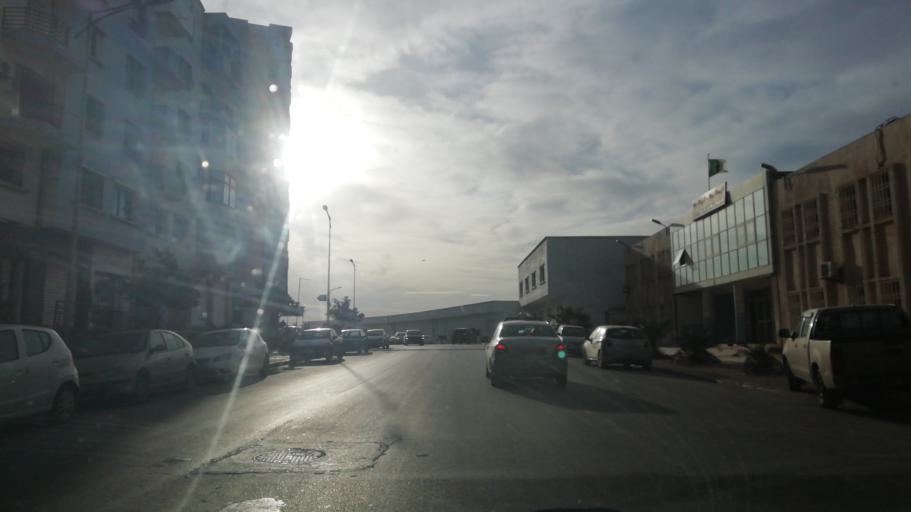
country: DZ
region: Oran
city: Bir el Djir
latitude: 35.7223
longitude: -0.5941
